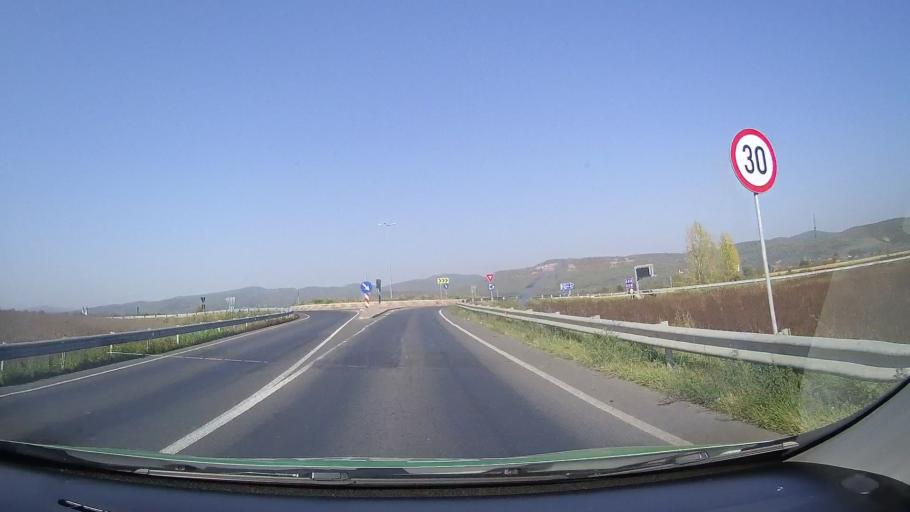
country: RO
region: Hunedoara
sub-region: Comuna Ilia
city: Ilia
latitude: 45.9436
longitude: 22.6250
